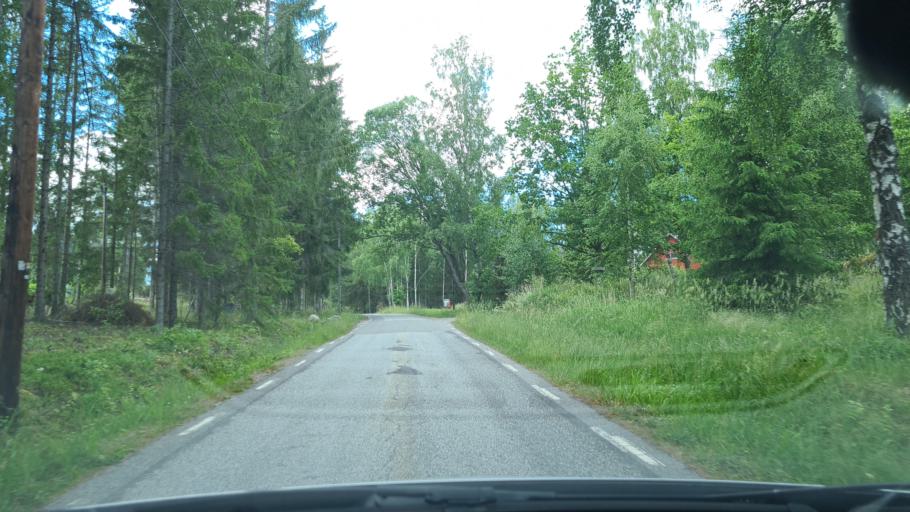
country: SE
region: Stockholm
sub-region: Vaxholms Kommun
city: Vaxholm
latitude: 59.4165
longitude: 18.4352
